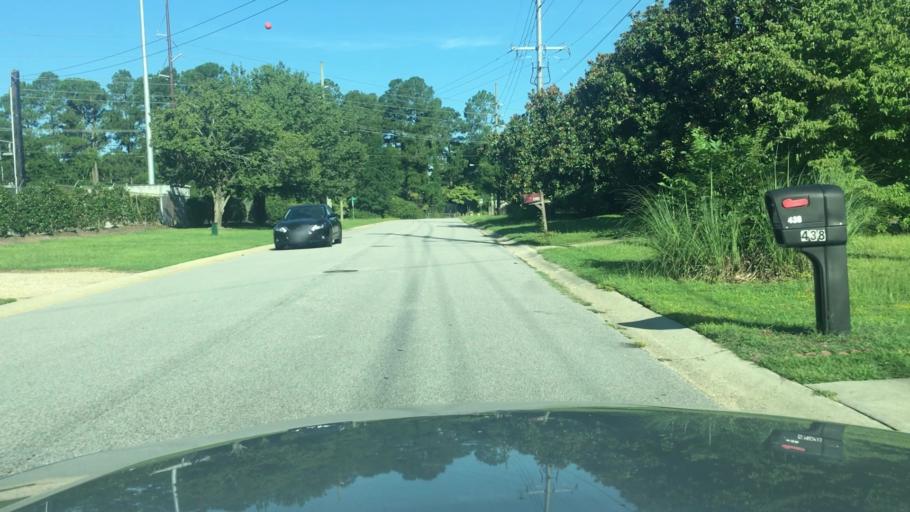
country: US
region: North Carolina
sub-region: Cumberland County
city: Fayetteville
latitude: 35.1315
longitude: -78.8914
